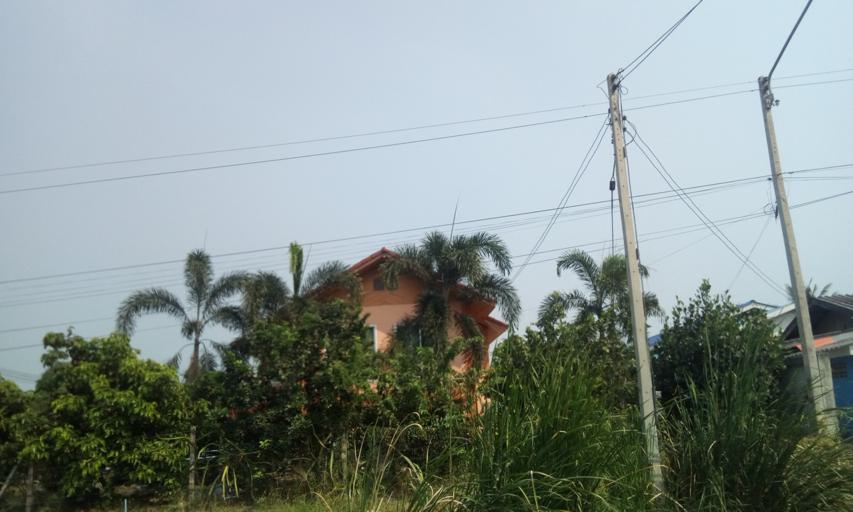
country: TH
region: Pathum Thani
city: Lam Luk Ka
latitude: 13.9609
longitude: 100.7253
